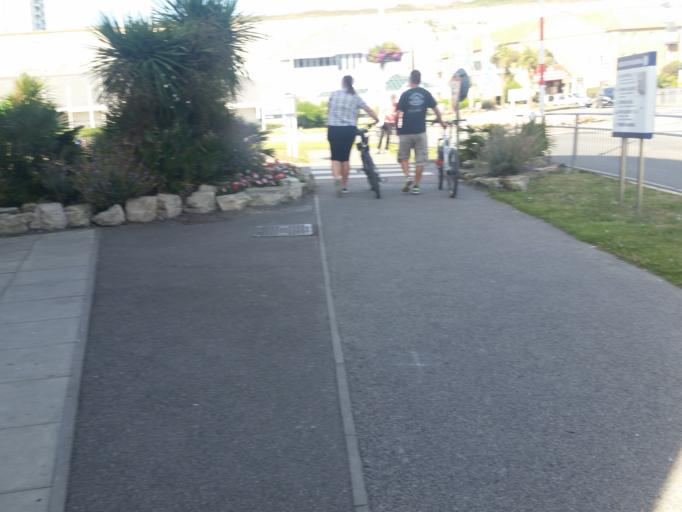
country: GB
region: England
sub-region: Brighton and Hove
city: Brighton
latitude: 50.8124
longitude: -0.1040
